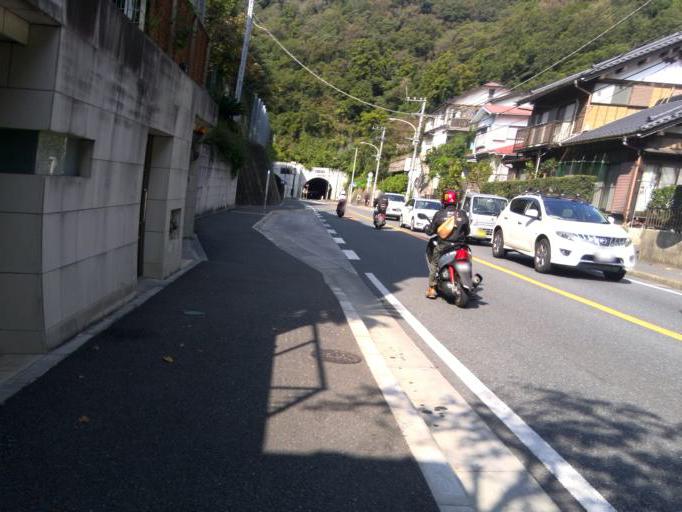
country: JP
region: Kanagawa
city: Zushi
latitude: 35.2847
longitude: 139.5802
